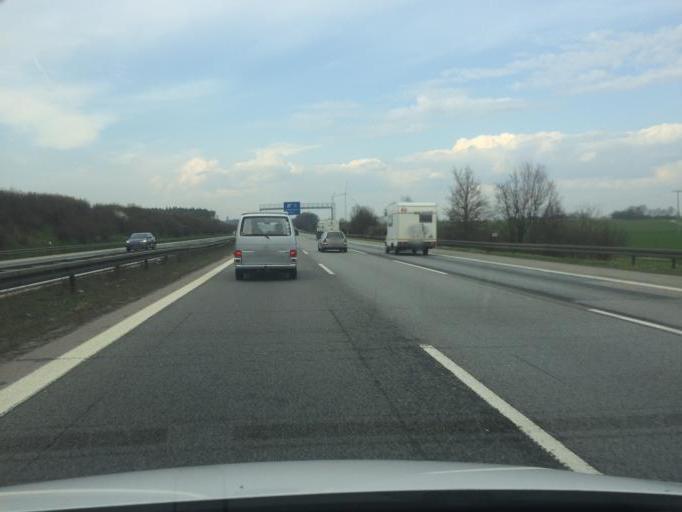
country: DE
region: Bavaria
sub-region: Regierungsbezirk Mittelfranken
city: Thalmassing
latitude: 49.1481
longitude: 11.2670
